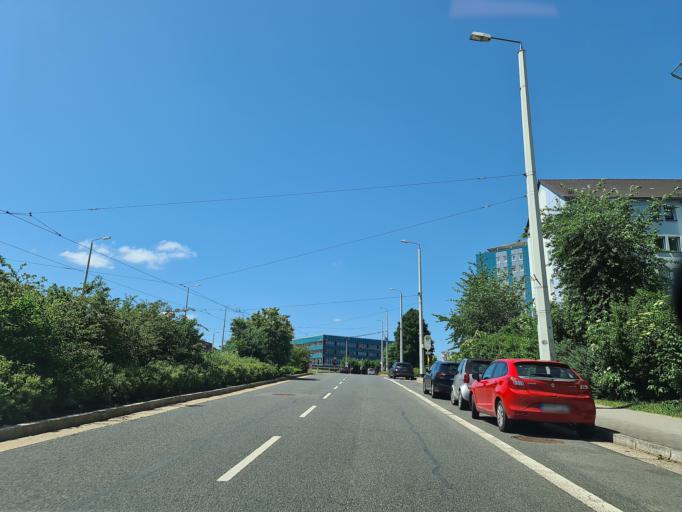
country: DE
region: Saxony
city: Plauen
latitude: 50.5038
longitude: 12.1329
